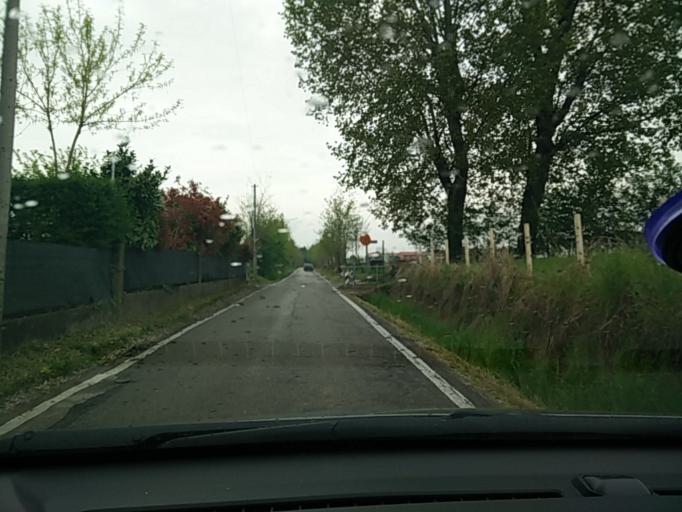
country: IT
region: Veneto
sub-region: Provincia di Treviso
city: Treviso
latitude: 45.6909
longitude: 12.2255
